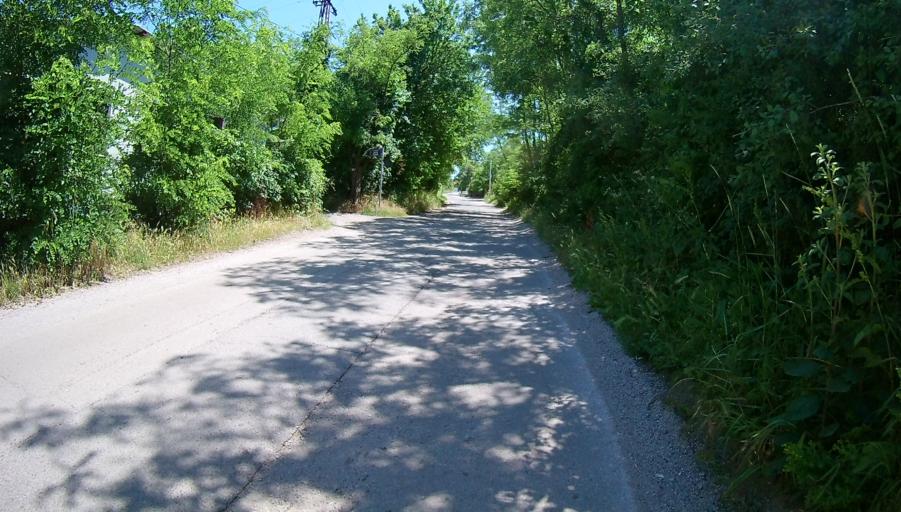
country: RS
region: Central Serbia
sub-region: Nisavski Okrug
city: Nis
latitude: 43.2955
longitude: 21.8983
